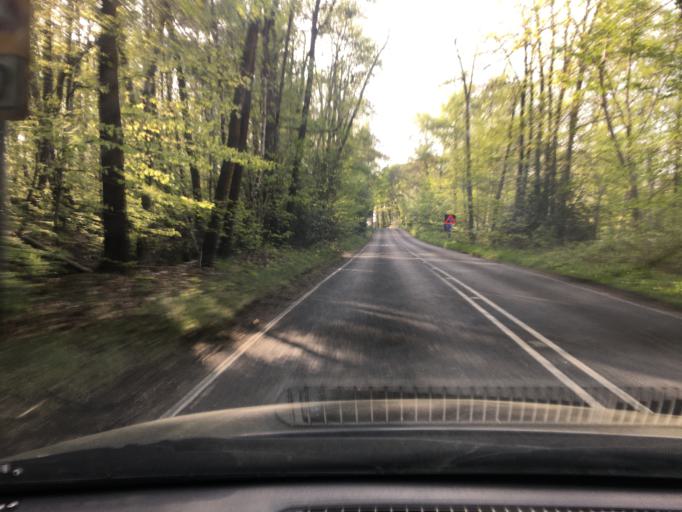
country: GB
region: England
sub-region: Bracknell Forest
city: Bracknell
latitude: 51.3877
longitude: -0.7595
